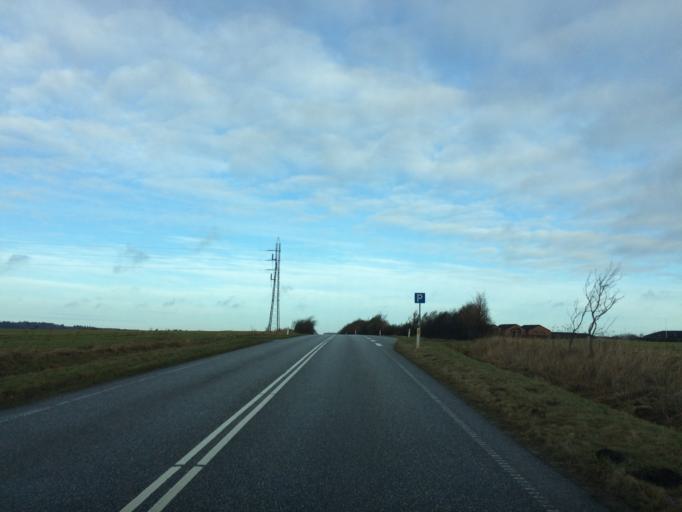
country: DK
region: Central Jutland
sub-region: Struer Kommune
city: Struer
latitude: 56.4793
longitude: 8.5535
